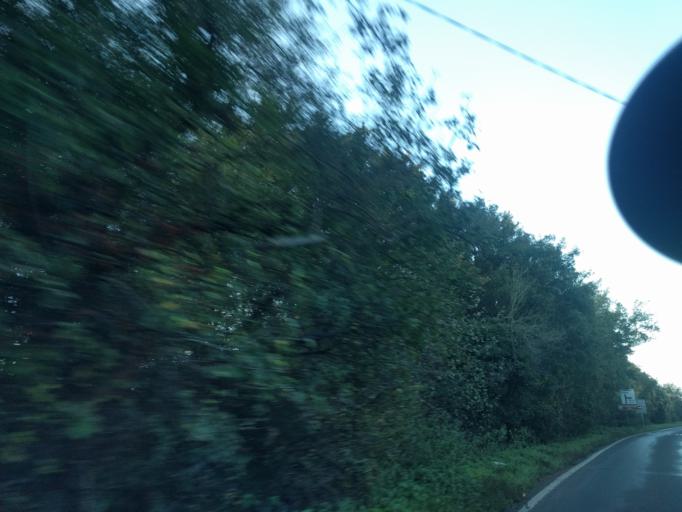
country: GB
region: England
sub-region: Essex
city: Rayne
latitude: 51.8390
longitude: 0.6080
